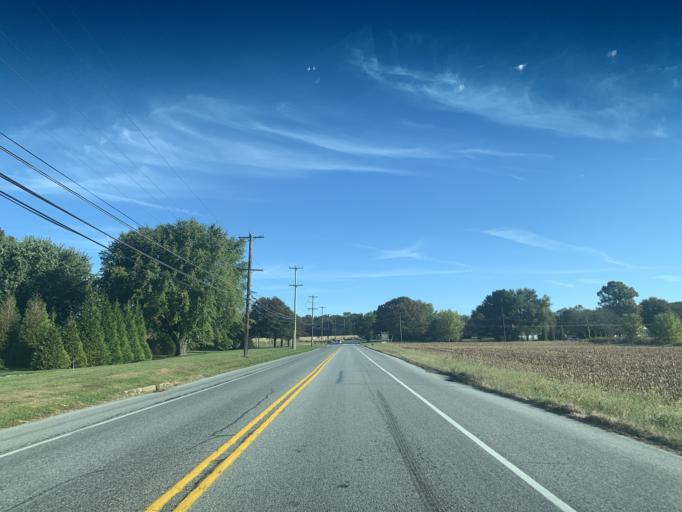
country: US
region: Pennsylvania
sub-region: Chester County
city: Oxford
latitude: 39.8193
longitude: -75.9650
